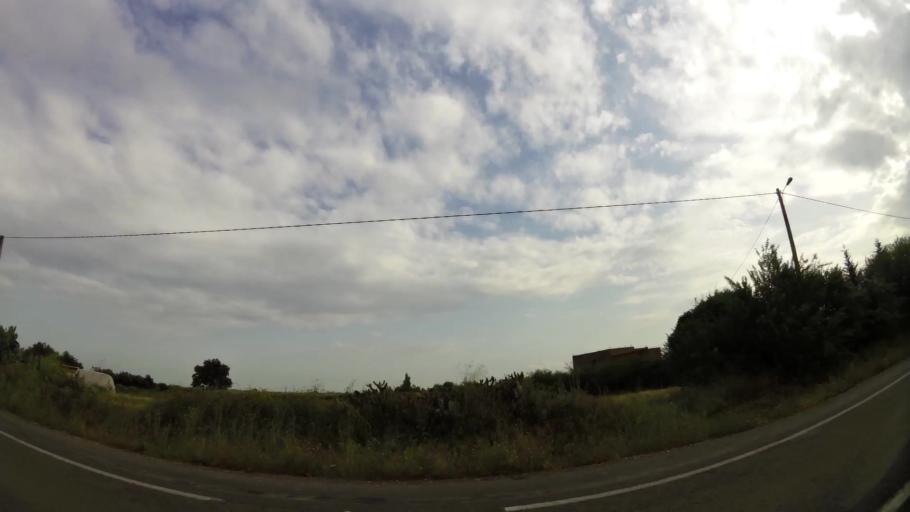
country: MA
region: Rabat-Sale-Zemmour-Zaer
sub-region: Khemisset
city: Khemisset
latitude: 33.7859
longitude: -6.1230
